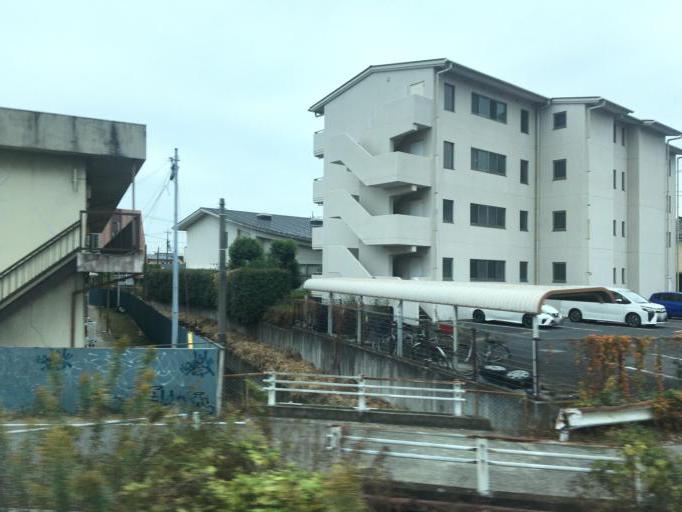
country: JP
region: Tochigi
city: Oyama
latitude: 36.3087
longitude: 139.8060
